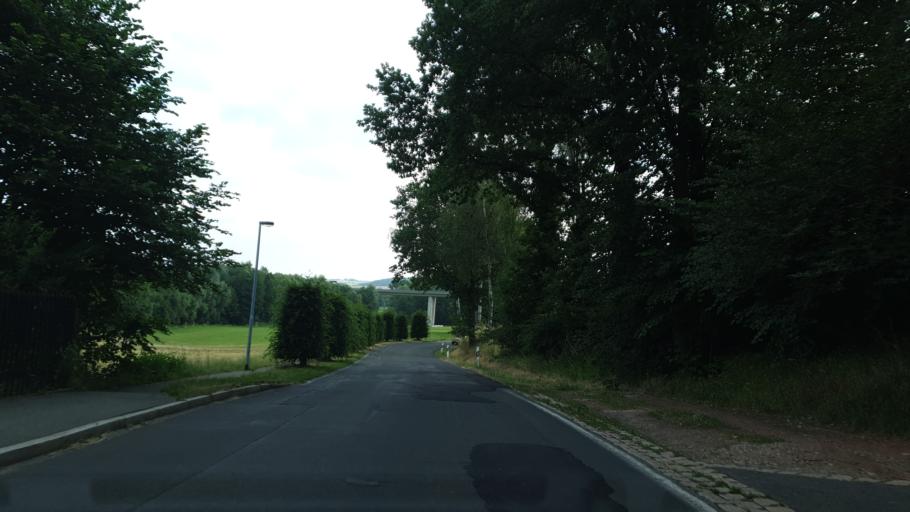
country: DE
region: Saxony
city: Lichtenstein
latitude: 50.7650
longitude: 12.6311
